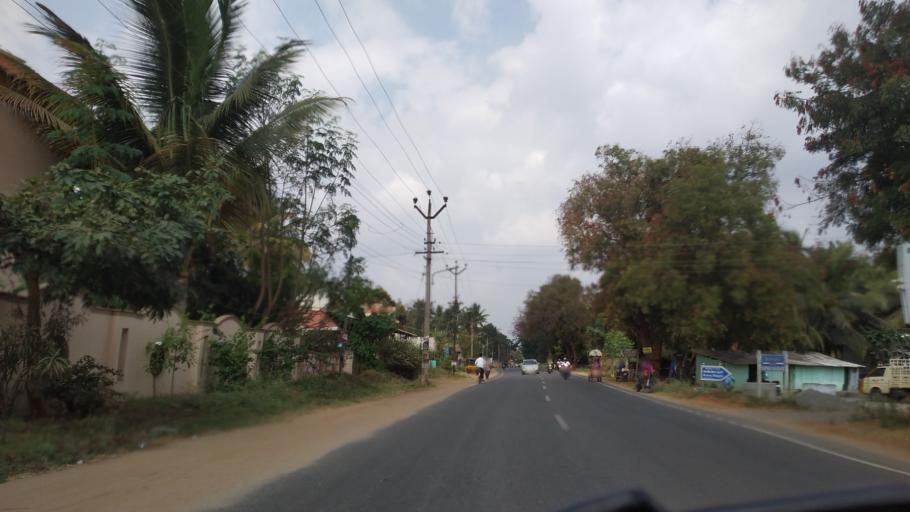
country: IN
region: Tamil Nadu
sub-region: Coimbatore
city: Perur
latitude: 10.9523
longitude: 76.9319
